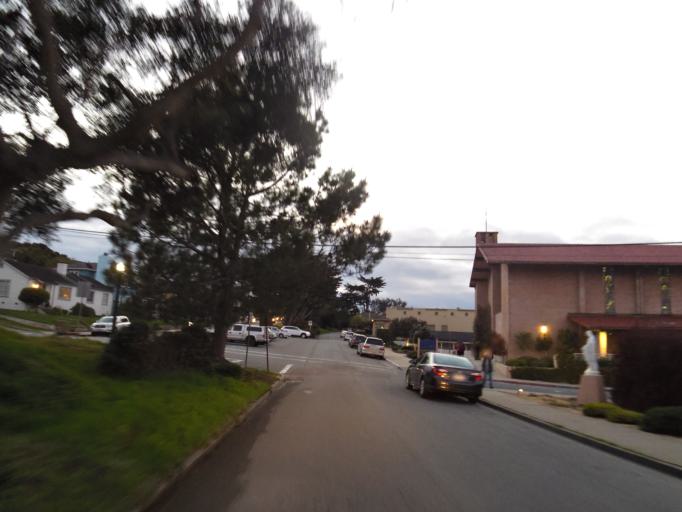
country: US
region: California
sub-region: Monterey County
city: Pacific Grove
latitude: 36.6192
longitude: -121.9117
